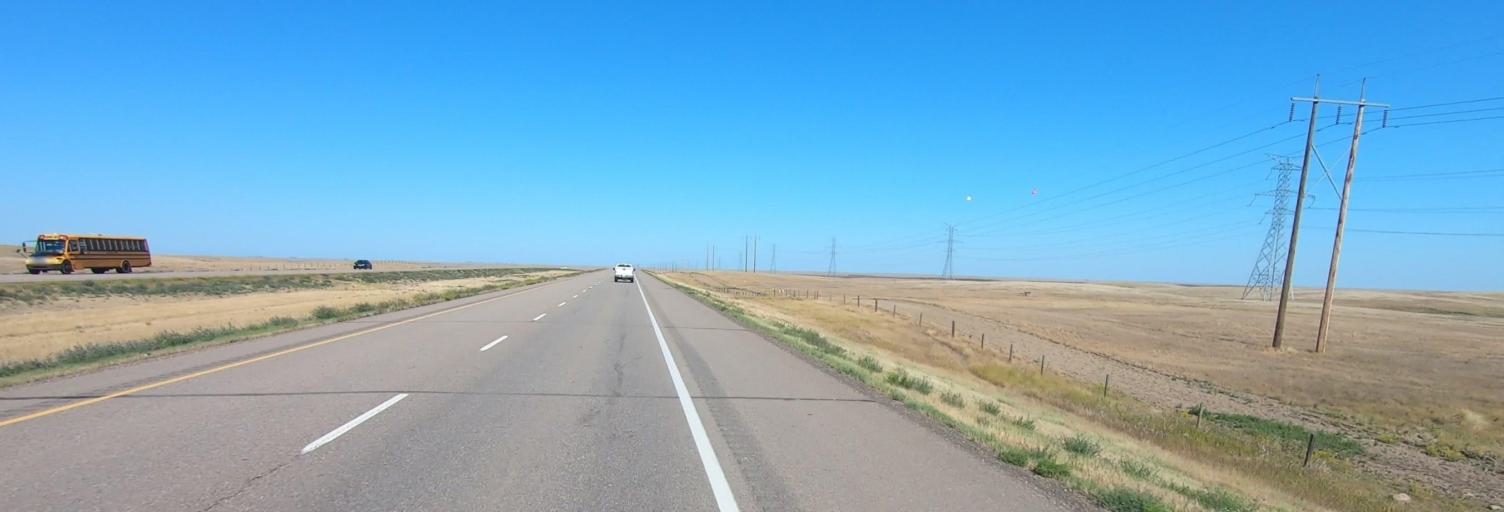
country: CA
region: Alberta
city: Bow Island
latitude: 50.3199
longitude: -111.3488
